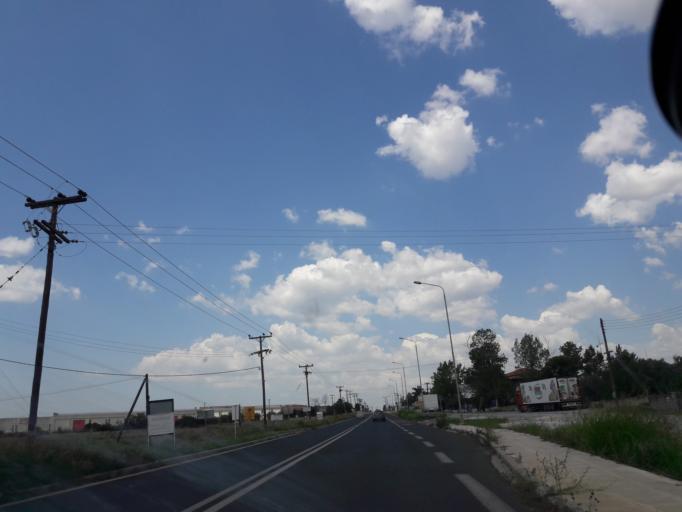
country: GR
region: Central Macedonia
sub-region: Nomos Thessalonikis
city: Thermi
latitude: 40.5283
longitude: 23.0451
